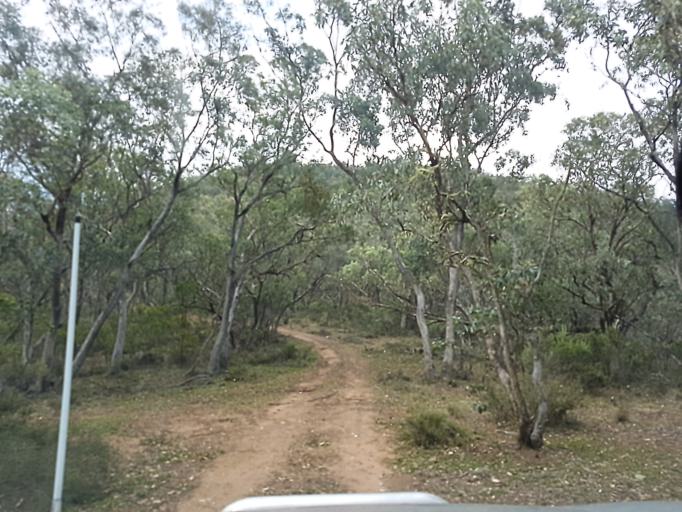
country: AU
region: New South Wales
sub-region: Snowy River
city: Jindabyne
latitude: -36.9932
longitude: 148.4090
